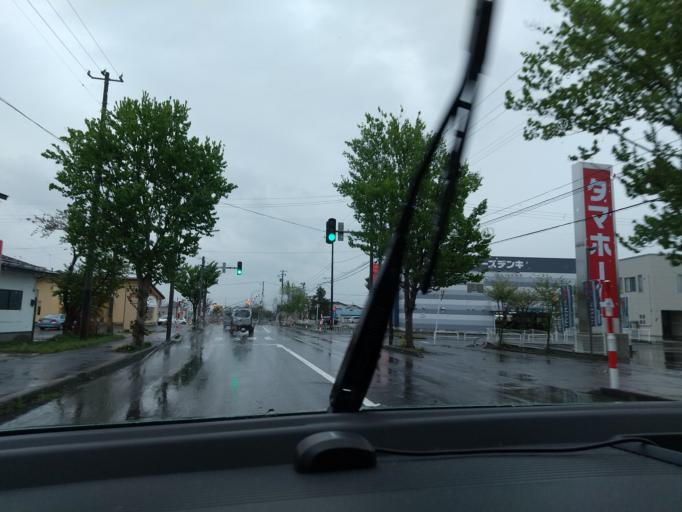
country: JP
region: Akita
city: Yokotemachi
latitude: 39.3018
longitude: 140.5500
